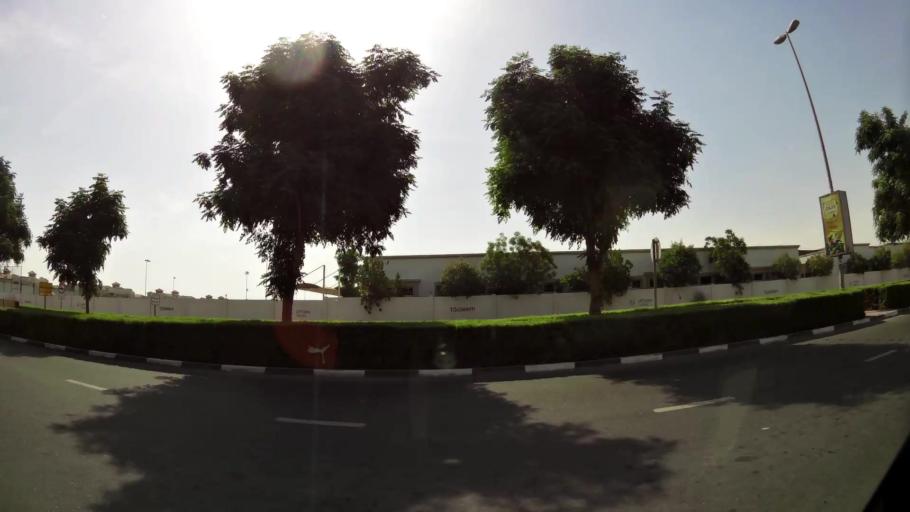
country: AE
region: Ash Shariqah
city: Sharjah
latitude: 25.2100
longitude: 55.4213
